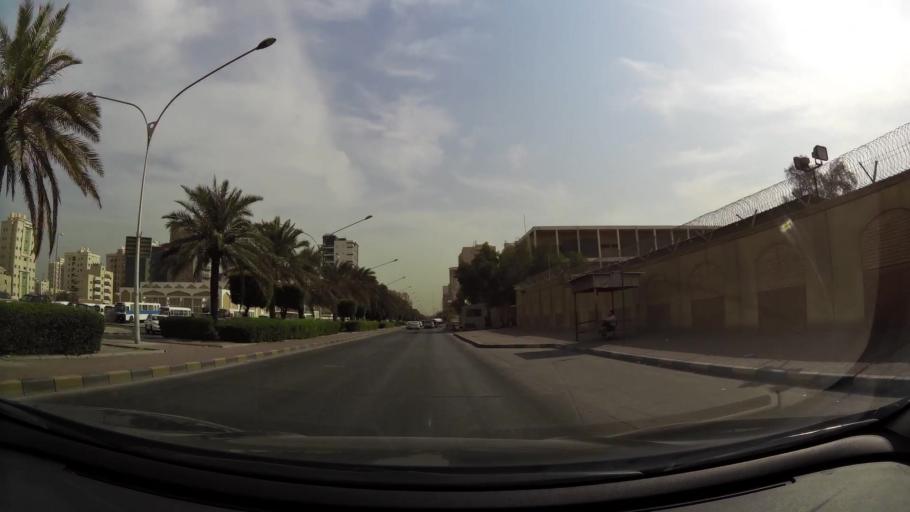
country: KW
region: Al Farwaniyah
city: Al Farwaniyah
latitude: 29.2824
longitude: 47.9702
